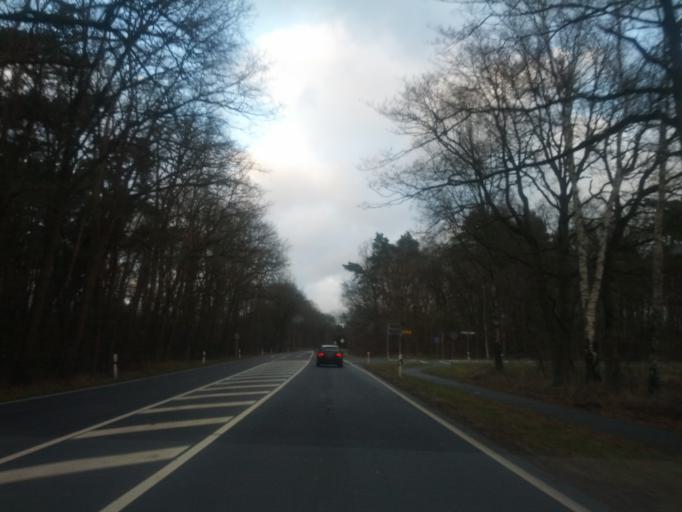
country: DE
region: Lower Saxony
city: Scheessel
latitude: 53.1467
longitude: 9.4601
